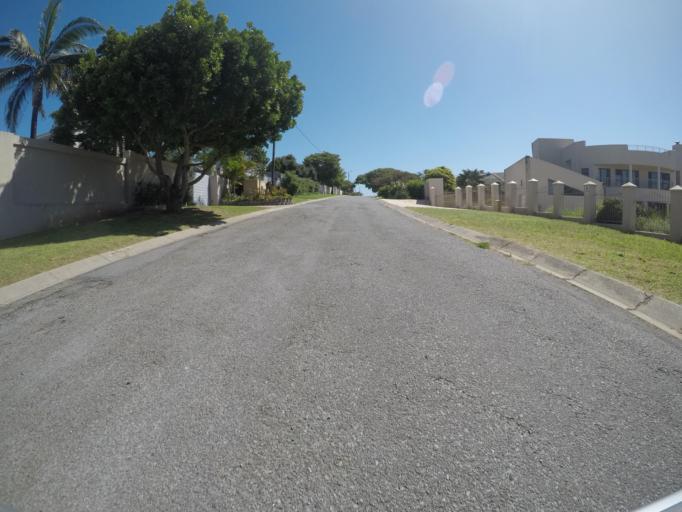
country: ZA
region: Eastern Cape
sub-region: Buffalo City Metropolitan Municipality
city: East London
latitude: -32.9870
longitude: 27.9410
